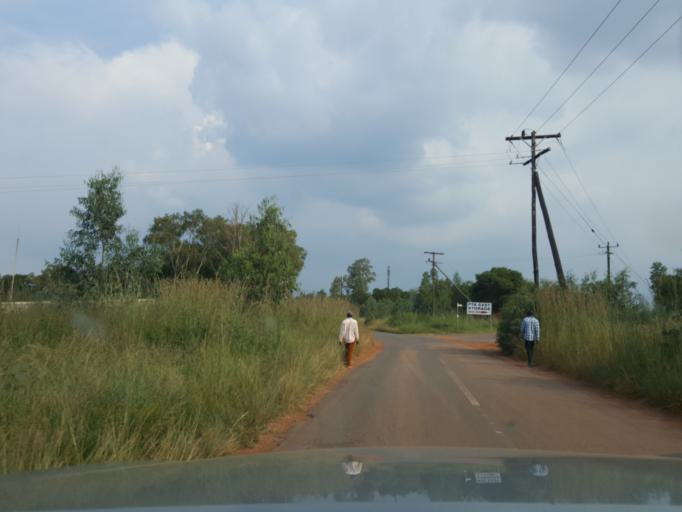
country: ZA
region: Gauteng
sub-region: City of Tshwane Metropolitan Municipality
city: Centurion
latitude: -25.8627
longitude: 28.3281
